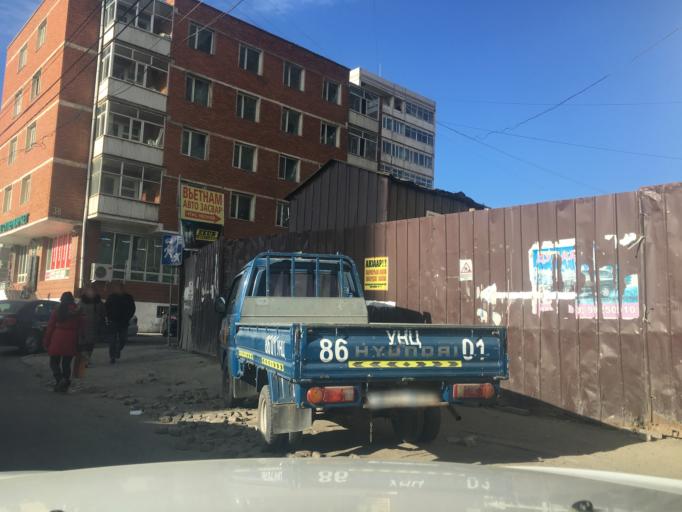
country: MN
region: Ulaanbaatar
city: Ulaanbaatar
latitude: 47.9184
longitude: 106.8872
